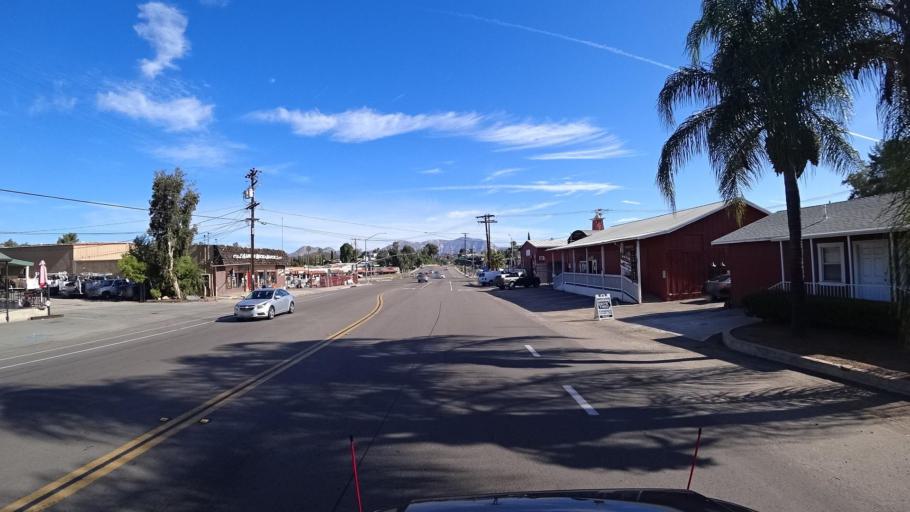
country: US
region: California
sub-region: San Diego County
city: Winter Gardens
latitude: 32.8316
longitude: -116.9061
